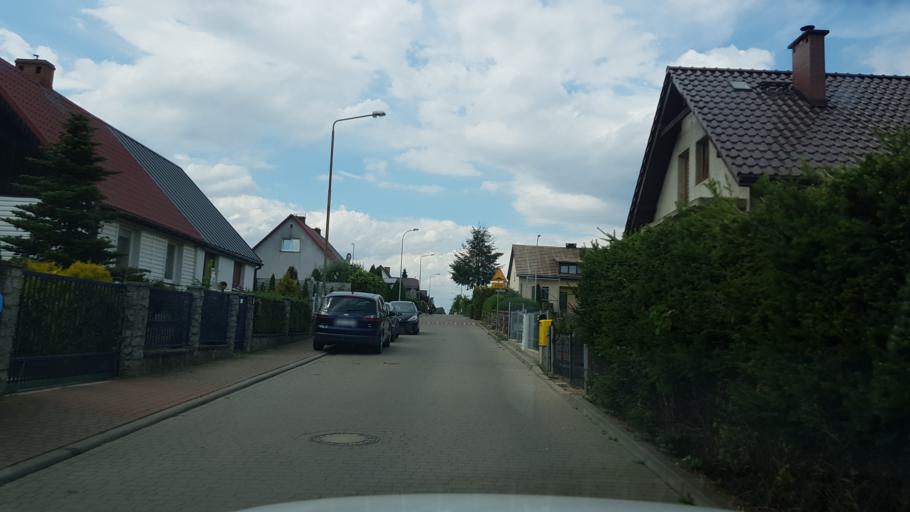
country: PL
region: West Pomeranian Voivodeship
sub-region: Powiat drawski
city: Drawsko Pomorskie
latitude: 53.5425
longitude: 15.8113
